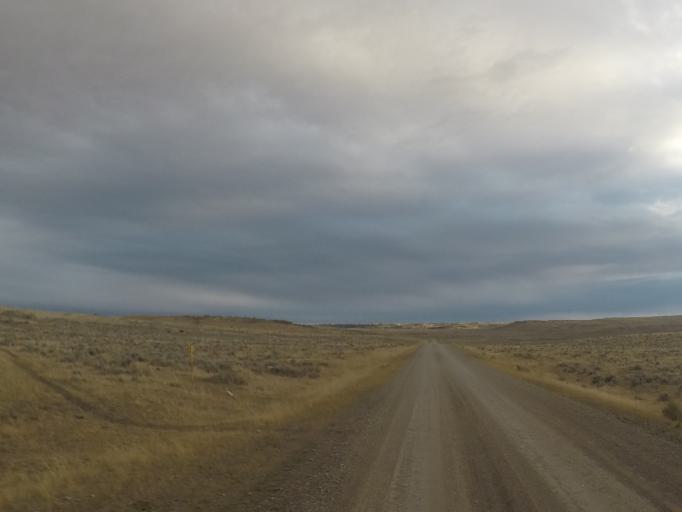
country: US
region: Montana
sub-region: Golden Valley County
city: Ryegate
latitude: 46.4671
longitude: -109.2645
